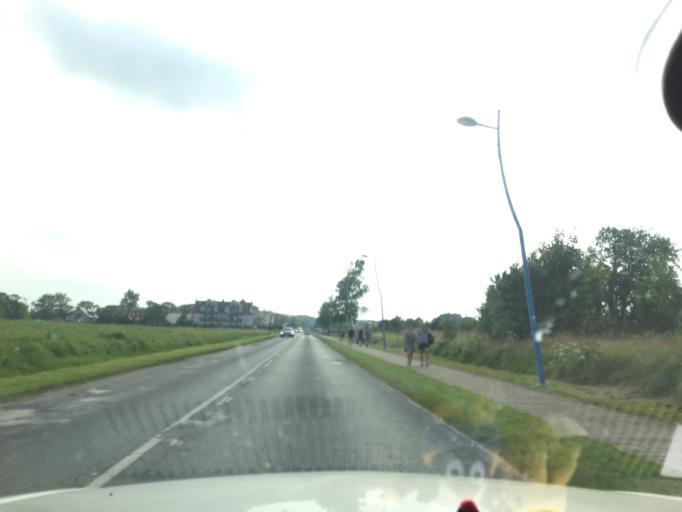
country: PL
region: West Pomeranian Voivodeship
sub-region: Powiat gryficki
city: Rewal
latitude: 54.0789
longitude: 15.0027
